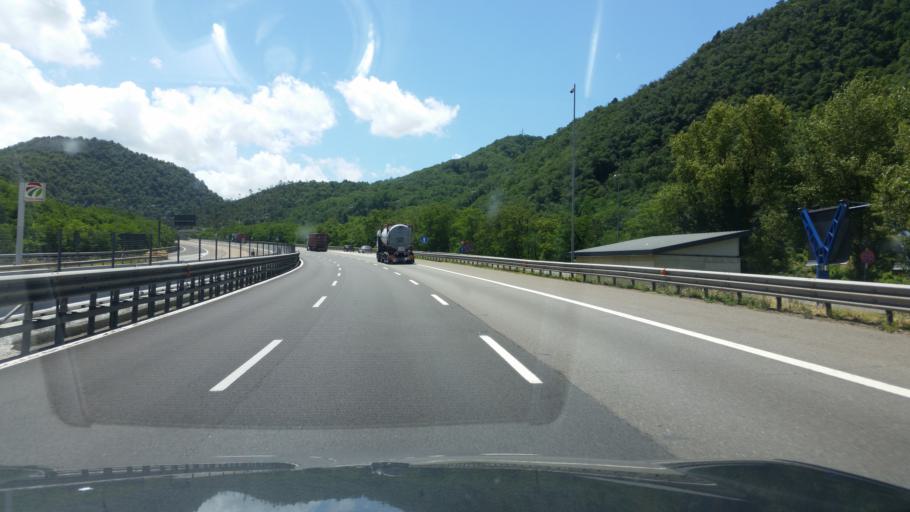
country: IT
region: Liguria
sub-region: Provincia di Genova
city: Rossiglione
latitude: 44.5913
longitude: 8.6648
